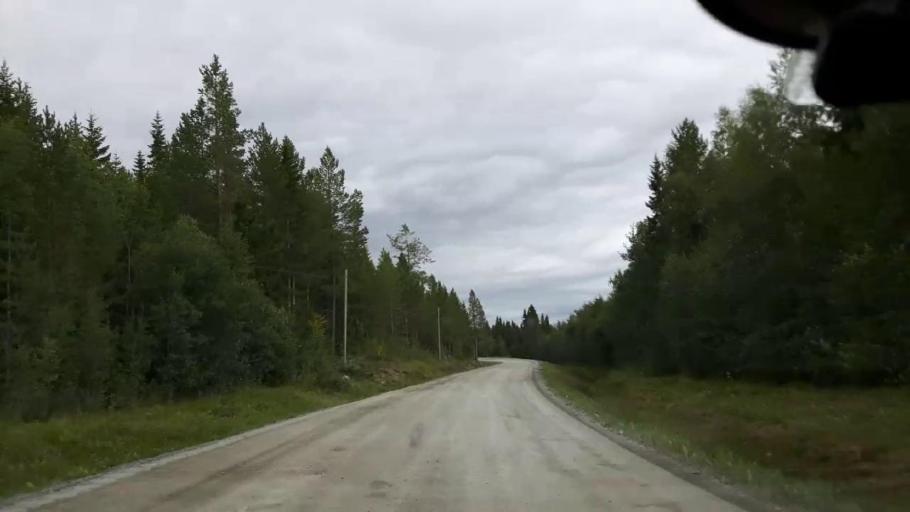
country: SE
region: Jaemtland
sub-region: OEstersunds Kommun
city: Brunflo
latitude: 63.1048
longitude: 15.0463
